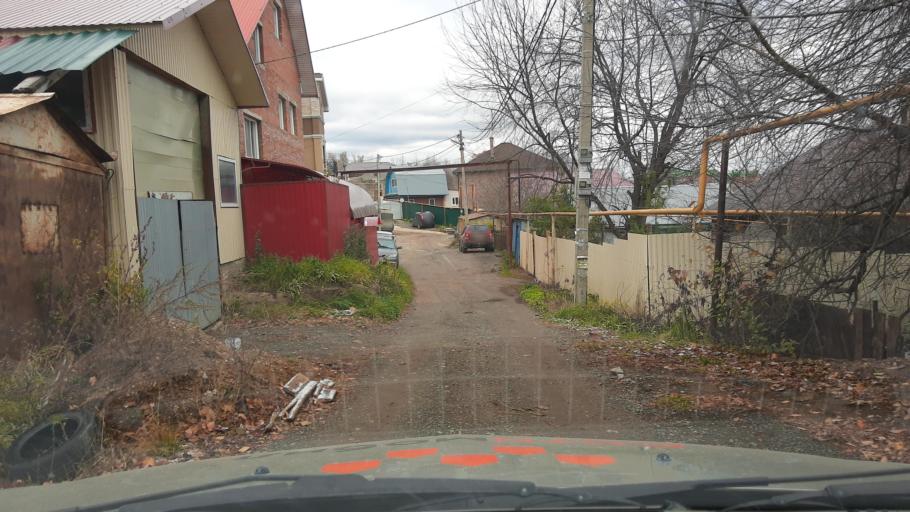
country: RU
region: Bashkortostan
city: Ufa
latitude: 54.7598
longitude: 56.0431
